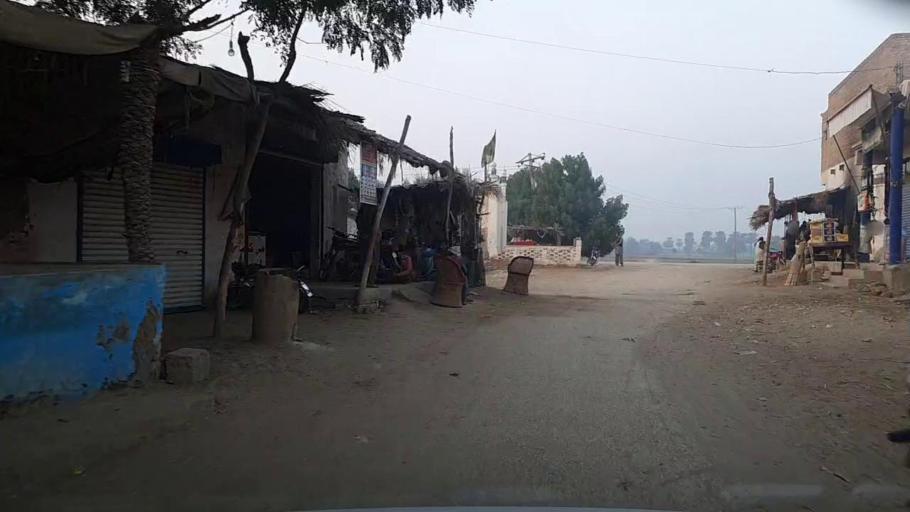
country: PK
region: Sindh
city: Bozdar
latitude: 27.0729
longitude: 68.5980
